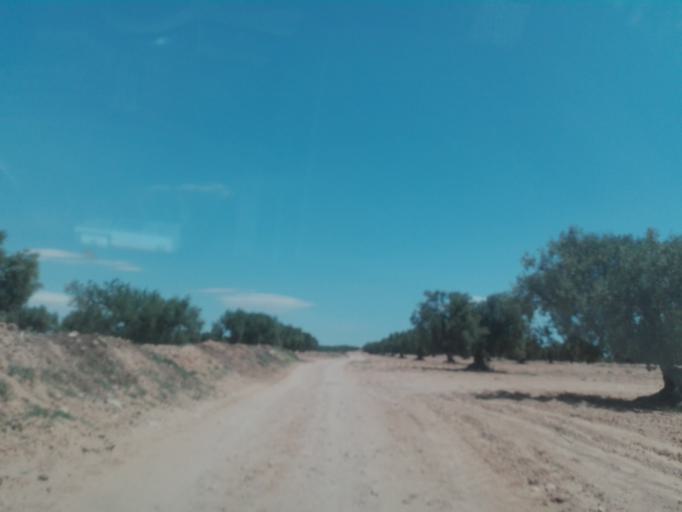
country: TN
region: Safaqis
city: Sfax
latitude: 34.6596
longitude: 10.6011
